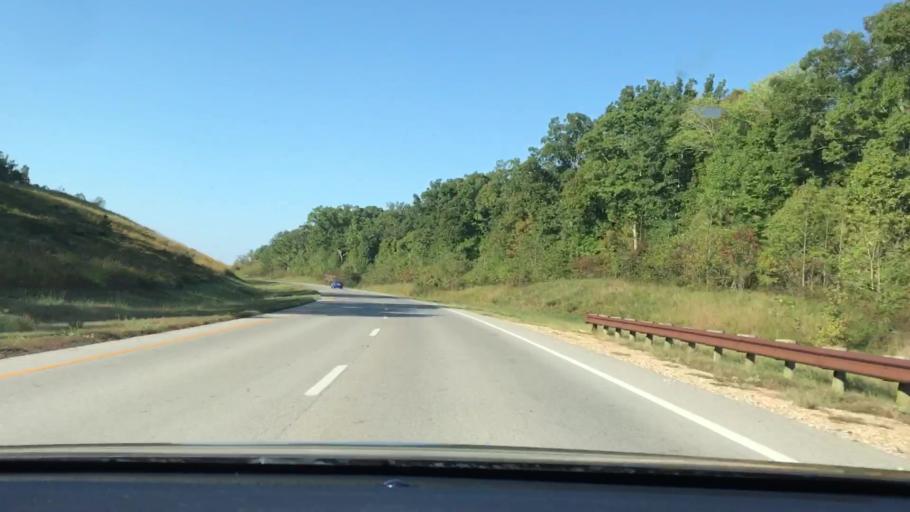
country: US
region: Kentucky
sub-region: Trigg County
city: Cadiz
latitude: 36.8026
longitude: -87.9918
